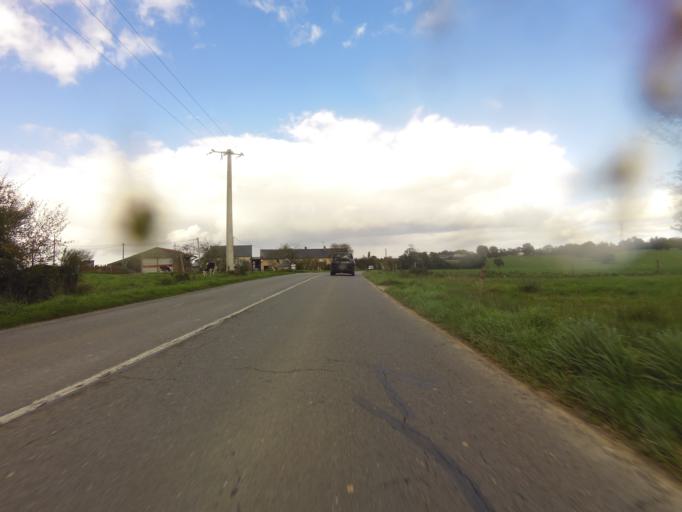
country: FR
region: Brittany
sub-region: Departement d'Ille-et-Vilaine
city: Erce-pres-Liffre
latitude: 48.2369
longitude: -1.5113
